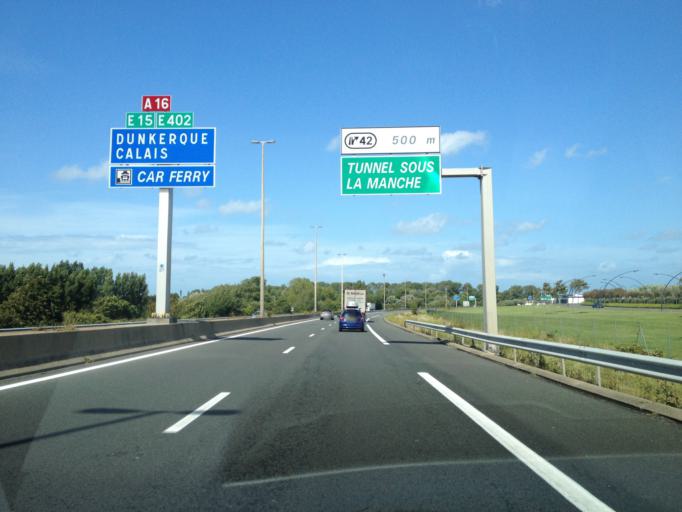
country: FR
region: Nord-Pas-de-Calais
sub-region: Departement du Pas-de-Calais
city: Coquelles
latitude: 50.9327
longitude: 1.8044
